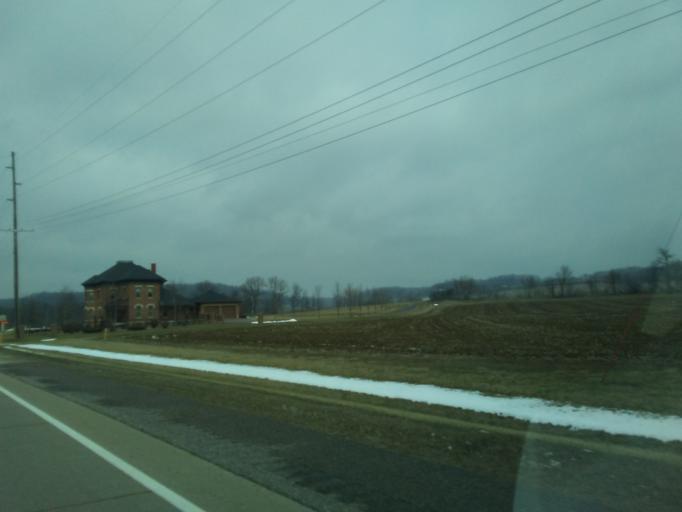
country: US
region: Wisconsin
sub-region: Richland County
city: Richland Center
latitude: 43.3094
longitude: -90.3382
